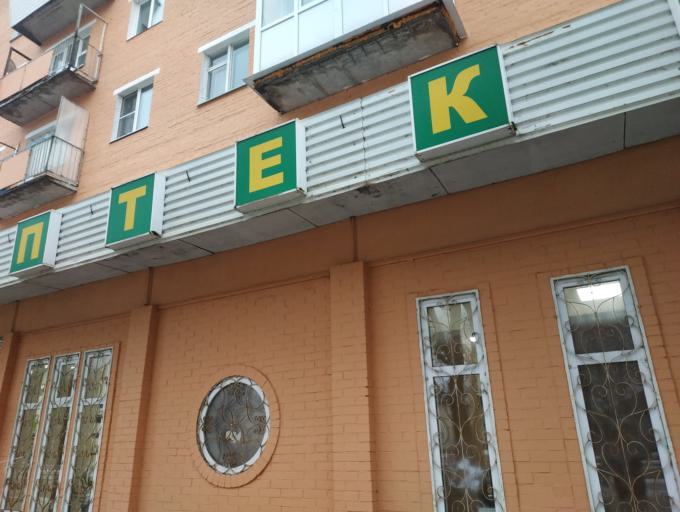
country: RU
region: Moskovskaya
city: Taldom
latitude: 56.7387
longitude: 37.5356
